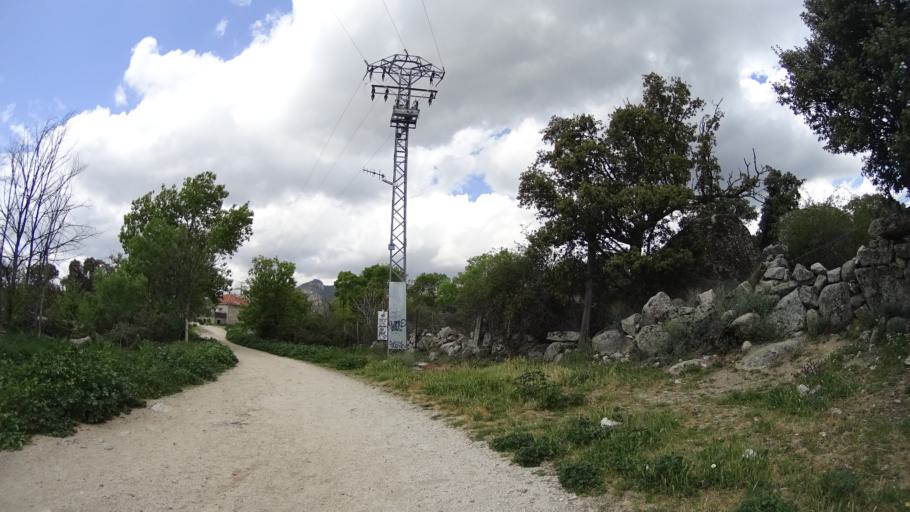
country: ES
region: Madrid
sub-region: Provincia de Madrid
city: Hoyo de Manzanares
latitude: 40.6202
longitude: -3.9026
